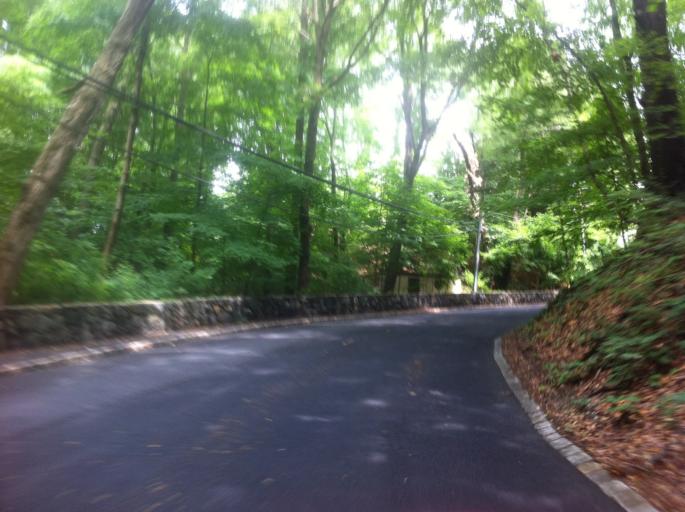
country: US
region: New York
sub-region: Nassau County
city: Bayville
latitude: 40.8938
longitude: -73.5619
